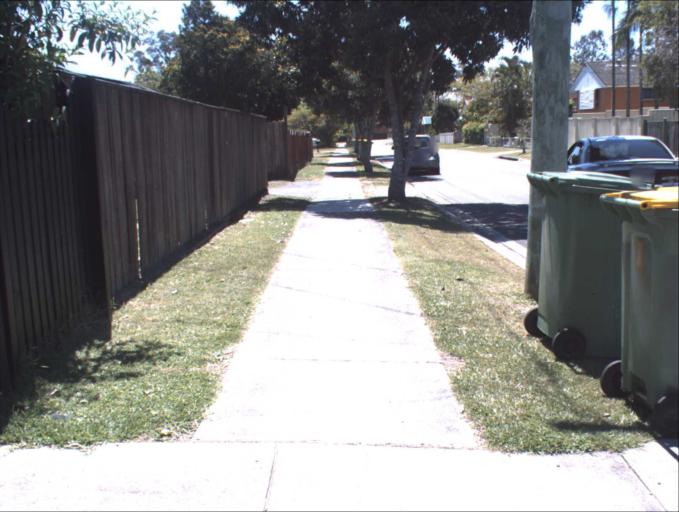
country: AU
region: Queensland
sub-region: Logan
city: Woodridge
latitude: -27.6252
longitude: 153.1084
